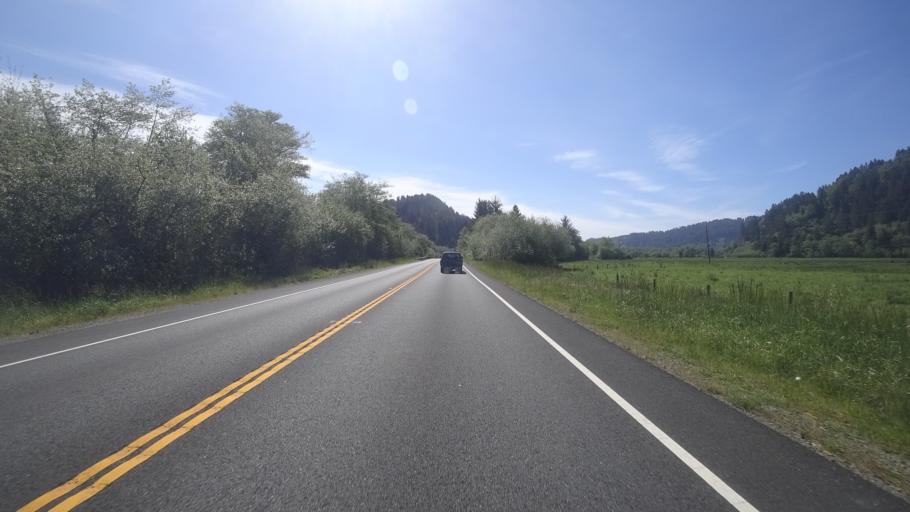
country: US
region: California
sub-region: Del Norte County
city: Bertsch-Oceanview
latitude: 41.5590
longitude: -124.0601
